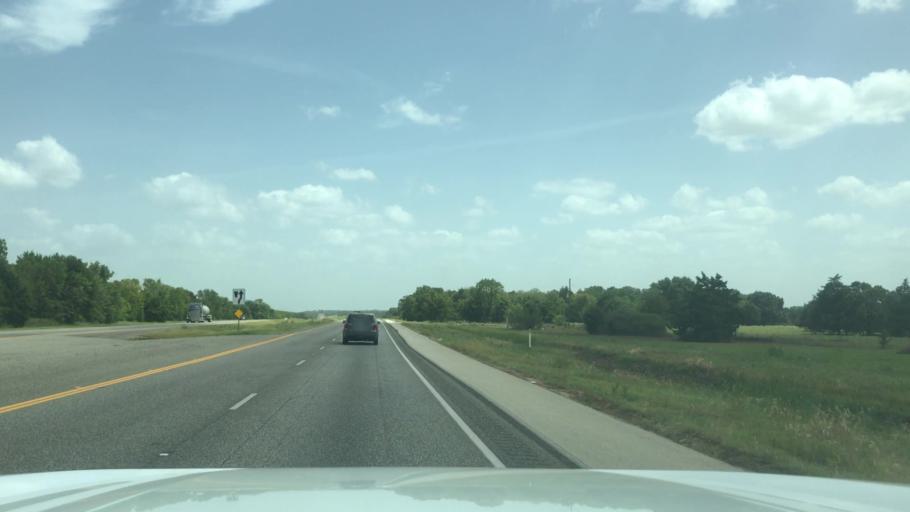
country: US
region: Texas
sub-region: Robertson County
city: Calvert
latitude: 30.9593
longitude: -96.6580
